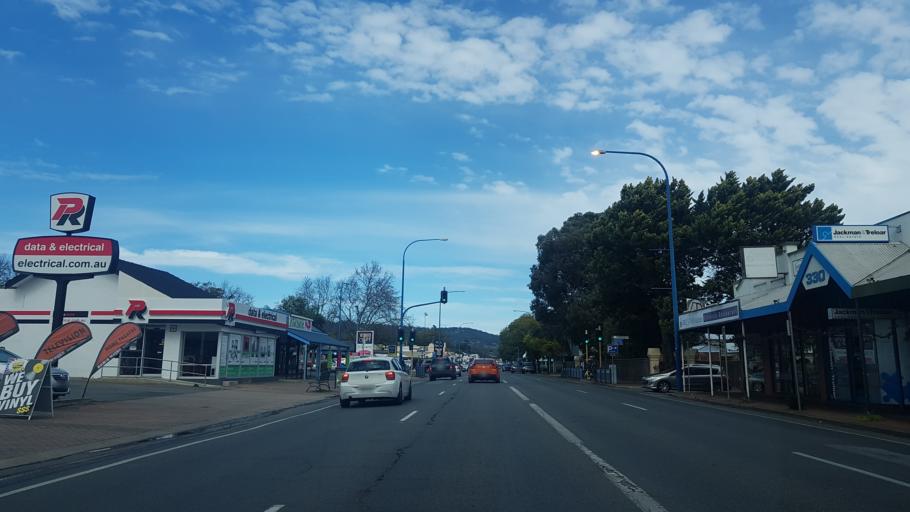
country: AU
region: South Australia
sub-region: Unley
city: Unley Park
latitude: -34.9579
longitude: 138.6081
